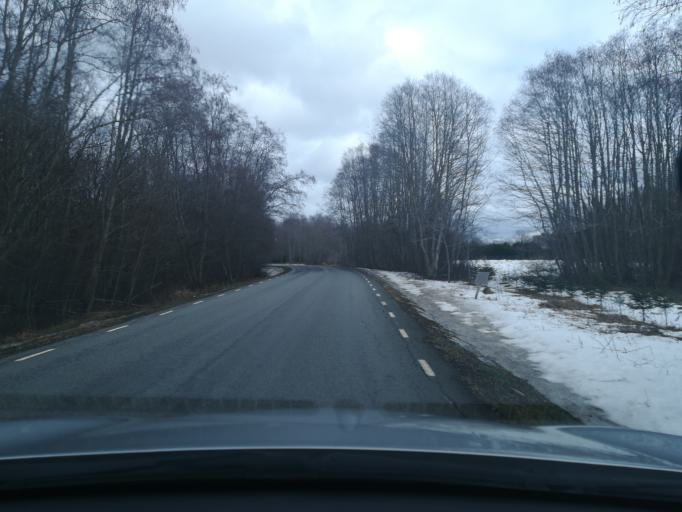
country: EE
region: Harju
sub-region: Saue linn
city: Saue
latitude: 59.3537
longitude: 24.5365
